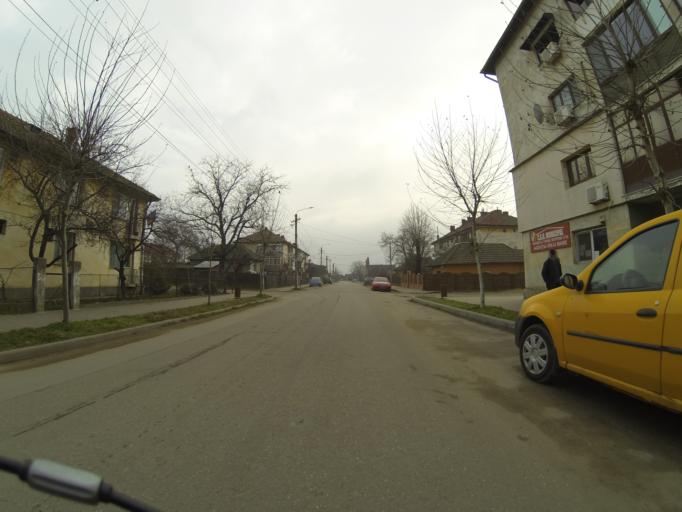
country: RO
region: Mehedinti
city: Vanju-Mare
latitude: 44.4237
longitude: 22.8723
